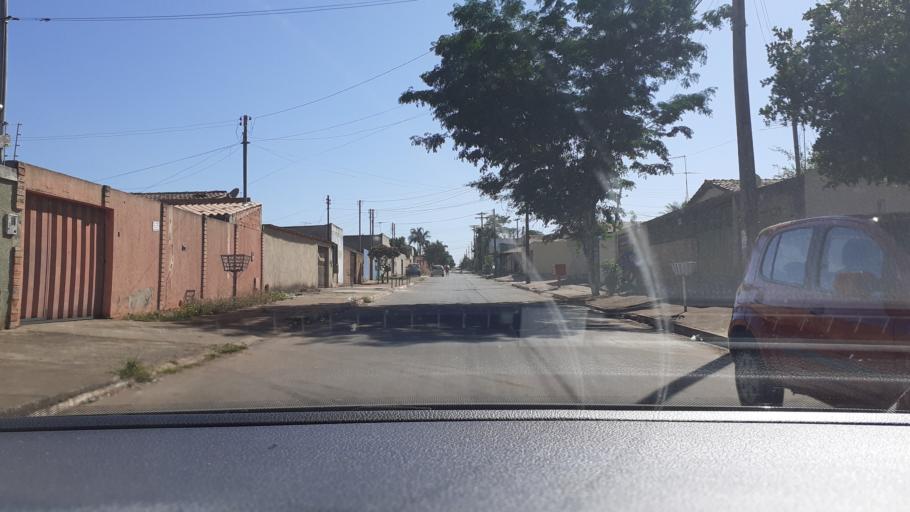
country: BR
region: Goias
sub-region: Aparecida De Goiania
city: Aparecida de Goiania
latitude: -16.8400
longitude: -49.2477
